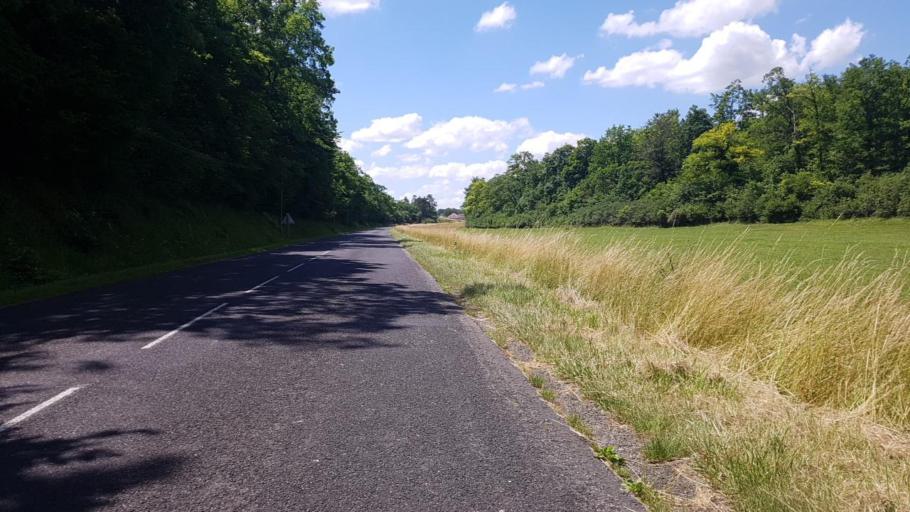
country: FR
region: Lorraine
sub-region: Departement de la Meuse
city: Vacon
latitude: 48.6694
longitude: 5.5572
